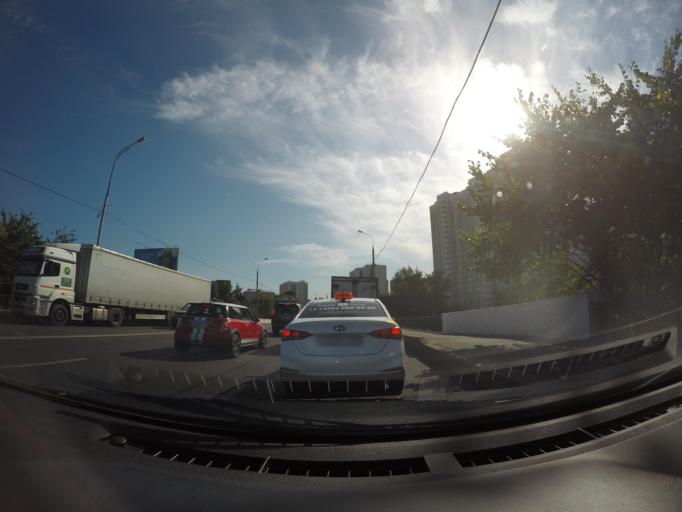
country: RU
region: Moscow
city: Mar'ina Roshcha
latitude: 55.8083
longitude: 37.6165
